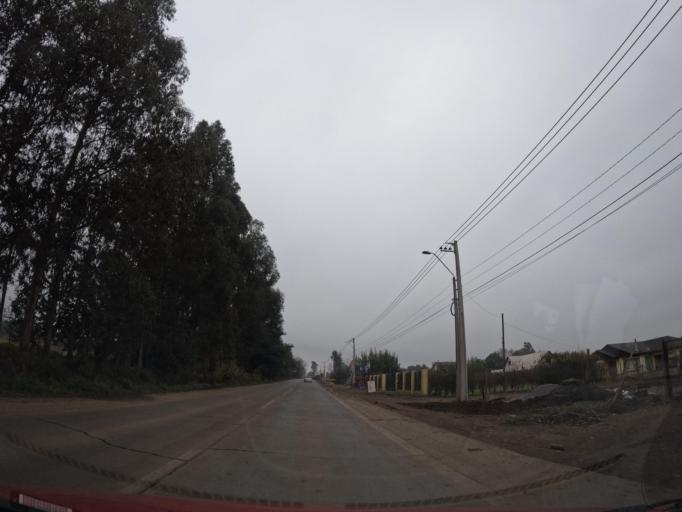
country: CL
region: Maule
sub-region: Provincia de Talca
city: San Clemente
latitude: -35.5688
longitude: -71.4400
